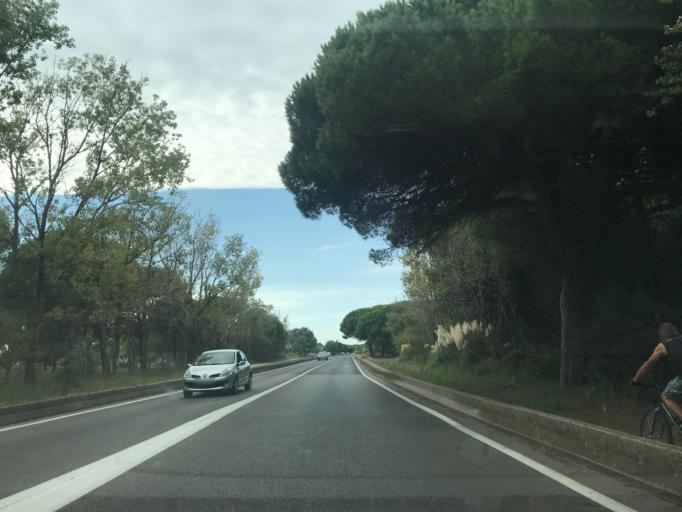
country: FR
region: Languedoc-Roussillon
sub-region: Departement du Gard
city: Le Grau-du-Roi
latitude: 43.5515
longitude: 4.1171
